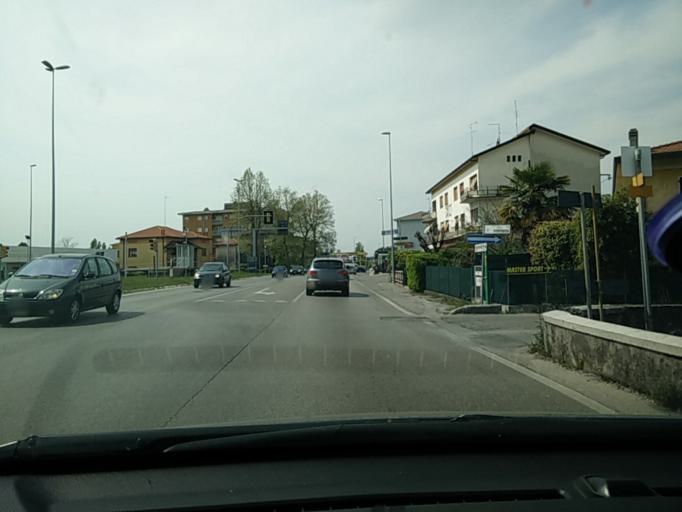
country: IT
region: Friuli Venezia Giulia
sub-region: Provincia di Pordenone
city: Porcia
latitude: 45.9681
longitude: 12.6266
